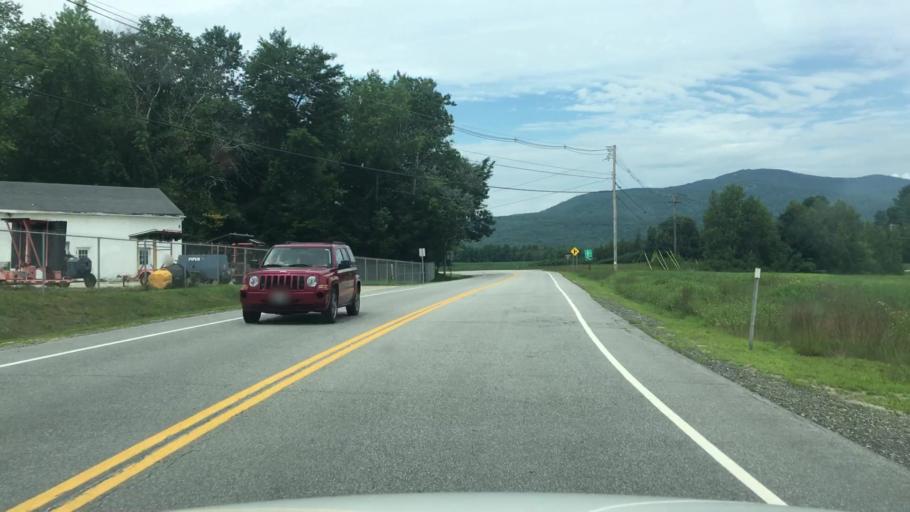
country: US
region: New Hampshire
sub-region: Grafton County
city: Plymouth
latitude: 43.7763
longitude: -71.7414
